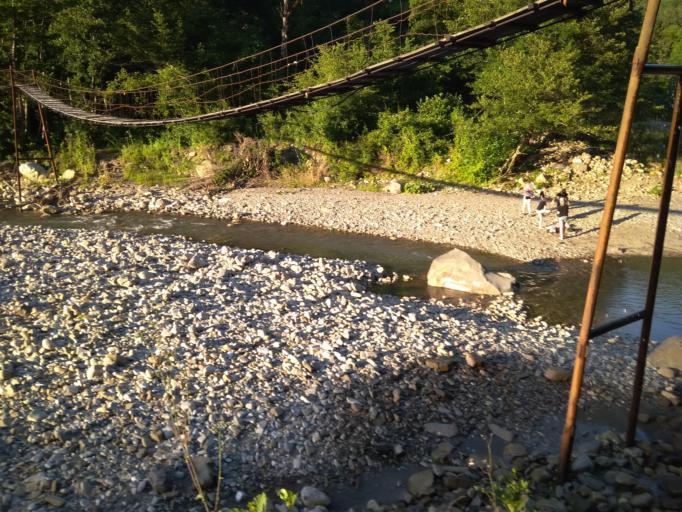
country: RU
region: Krasnodarskiy
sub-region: Sochi City
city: Lazarevskoye
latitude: 43.9992
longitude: 39.3968
